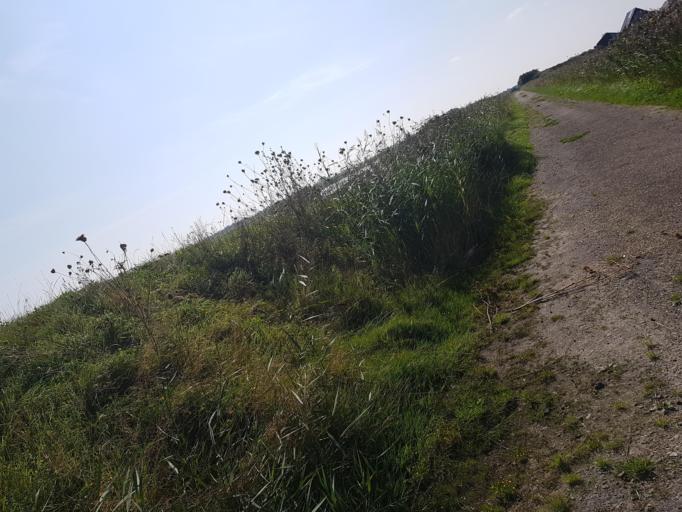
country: NL
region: North Holland
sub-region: Gemeente Texel
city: Den Burg
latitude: 53.1011
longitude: 4.8814
